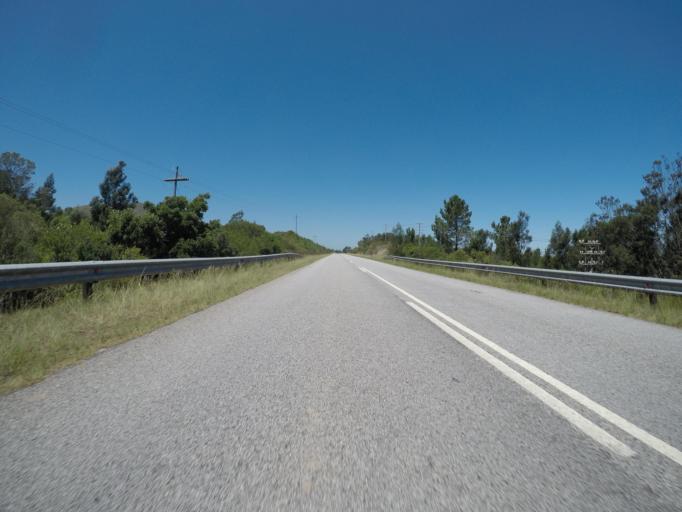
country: ZA
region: Eastern Cape
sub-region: Cacadu District Municipality
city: Kareedouw
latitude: -33.9596
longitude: 24.4142
